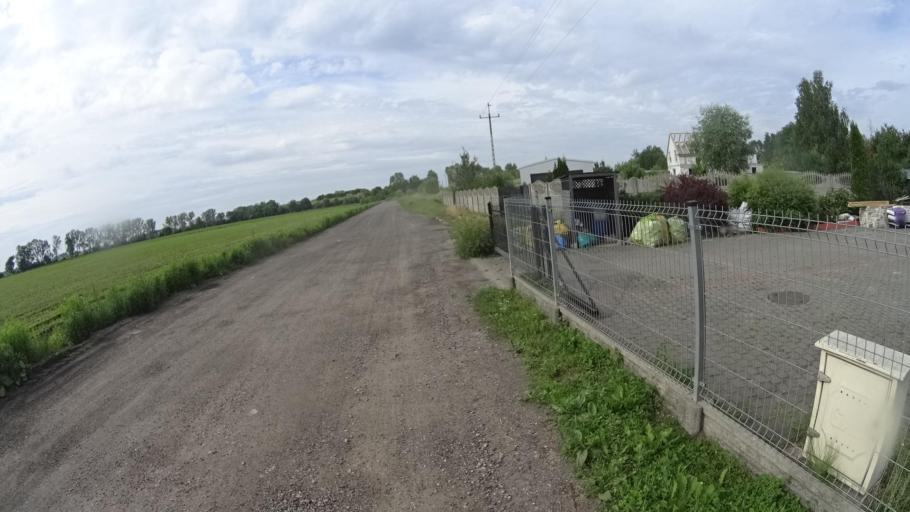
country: PL
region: Masovian Voivodeship
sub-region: Powiat warszawski zachodni
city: Jozefow
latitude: 52.1925
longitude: 20.7425
